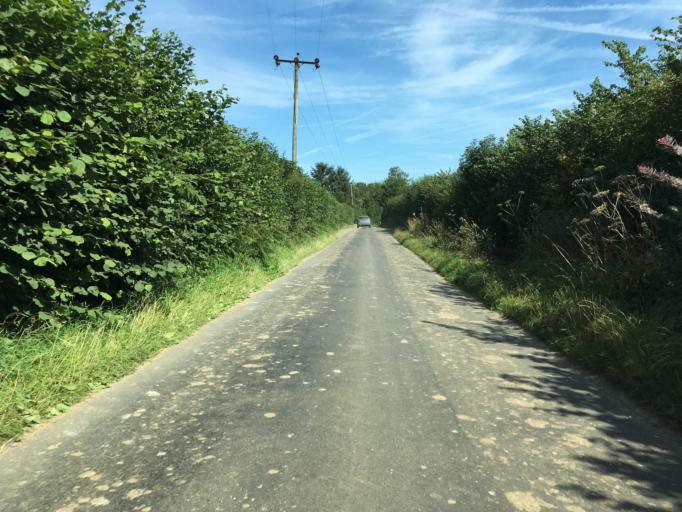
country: GB
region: England
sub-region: Hampshire
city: Highclere
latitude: 51.3124
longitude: -1.3846
